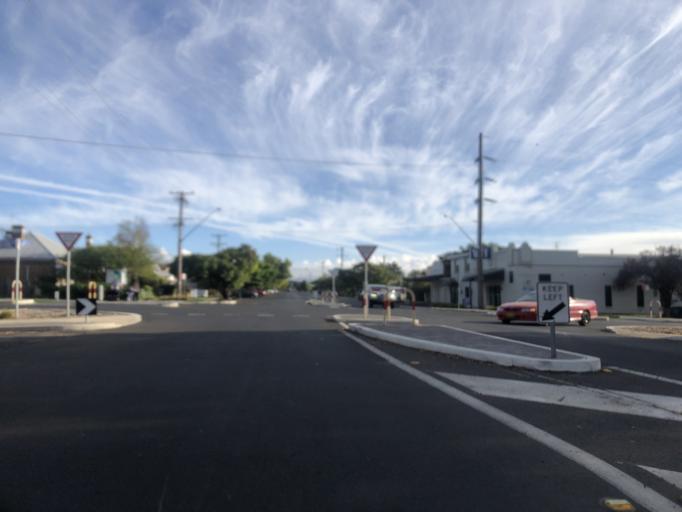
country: AU
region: New South Wales
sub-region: Orange Municipality
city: Orange
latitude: -33.2800
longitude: 149.1019
